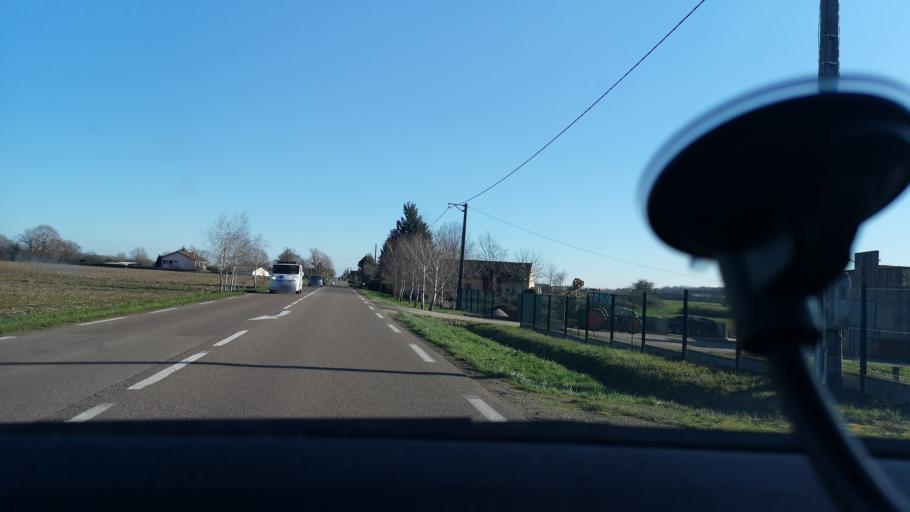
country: FR
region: Bourgogne
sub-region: Departement de Saone-et-Loire
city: Saint-Germain-du-Plain
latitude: 46.7551
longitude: 5.0145
